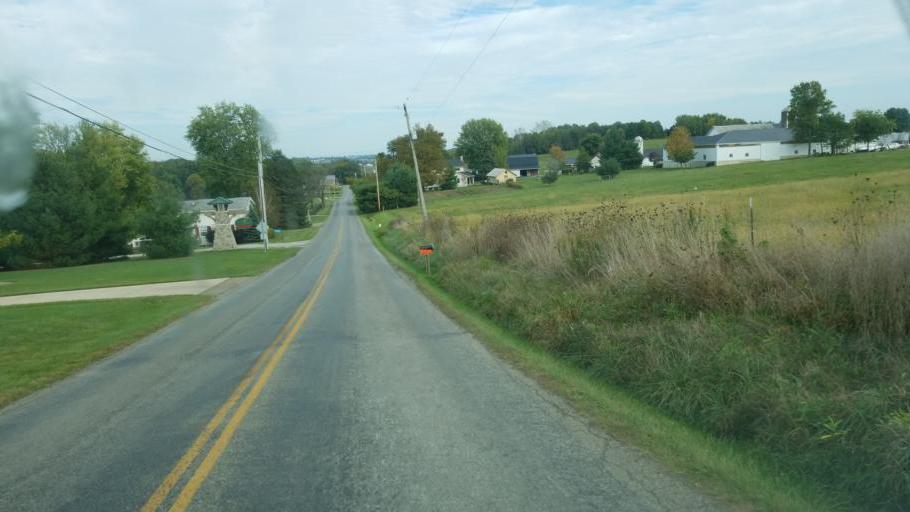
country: US
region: Ohio
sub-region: Holmes County
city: Millersburg
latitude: 40.5730
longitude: -81.8484
